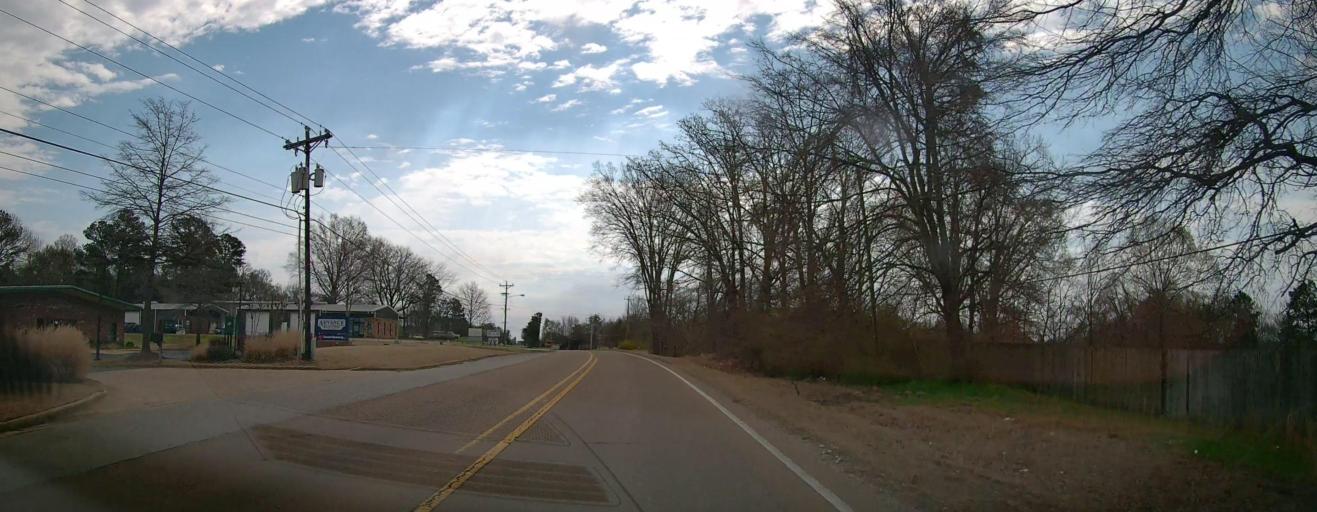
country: US
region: Mississippi
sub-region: De Soto County
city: Olive Branch
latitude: 34.9396
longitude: -89.8042
